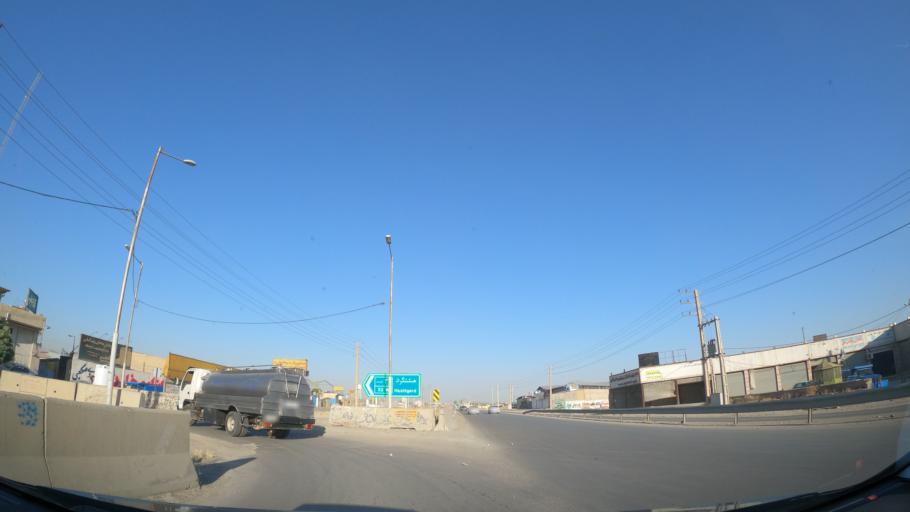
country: IR
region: Alborz
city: Hashtgerd
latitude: 35.9151
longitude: 50.7583
